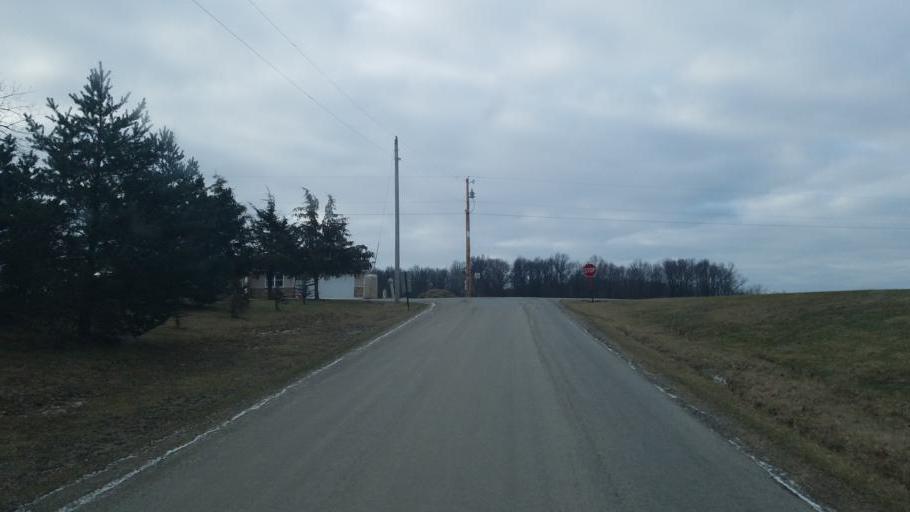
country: US
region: Ohio
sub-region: Morrow County
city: Mount Gilead
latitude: 40.5370
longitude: -82.7971
